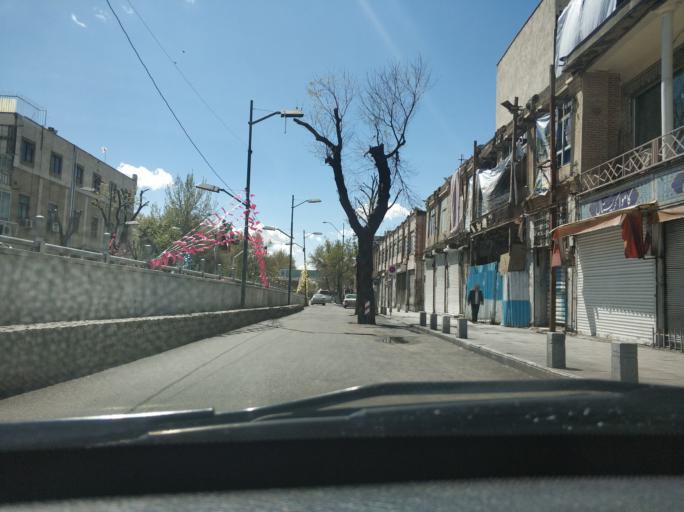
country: IR
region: Tehran
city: Tehran
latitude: 35.6857
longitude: 51.4099
